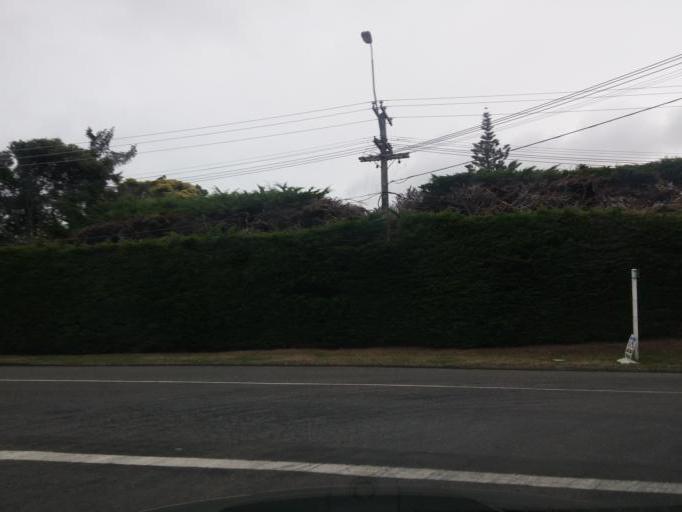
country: NZ
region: Wellington
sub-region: Kapiti Coast District
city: Paraparaumu
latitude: -40.8650
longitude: 175.0273
